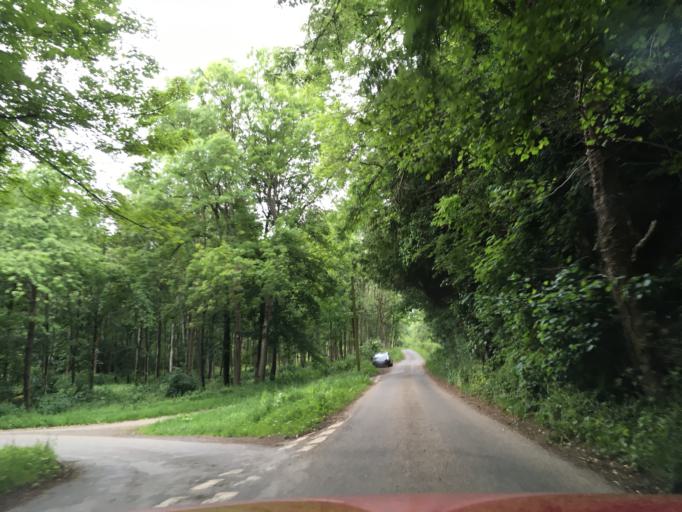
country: GB
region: England
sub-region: Wiltshire
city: Luckington
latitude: 51.5731
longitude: -2.2825
